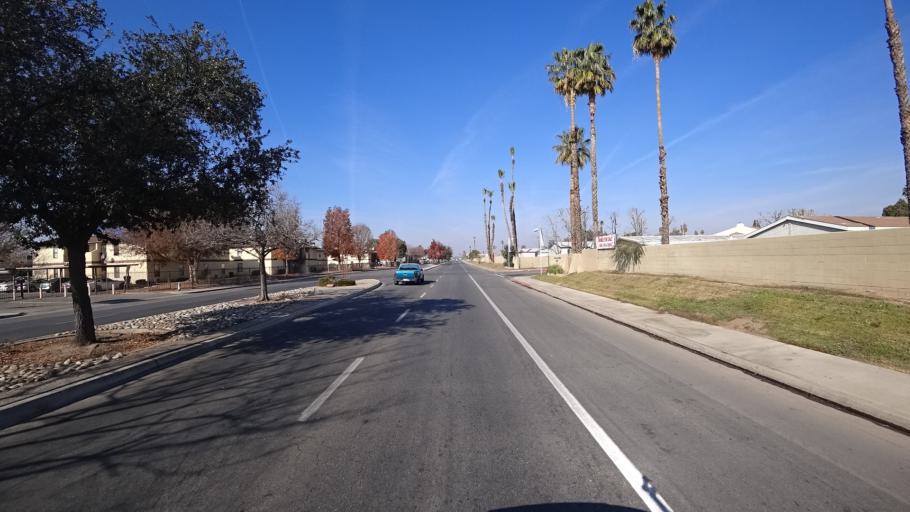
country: US
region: California
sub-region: Kern County
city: Bakersfield
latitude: 35.3262
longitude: -119.0100
